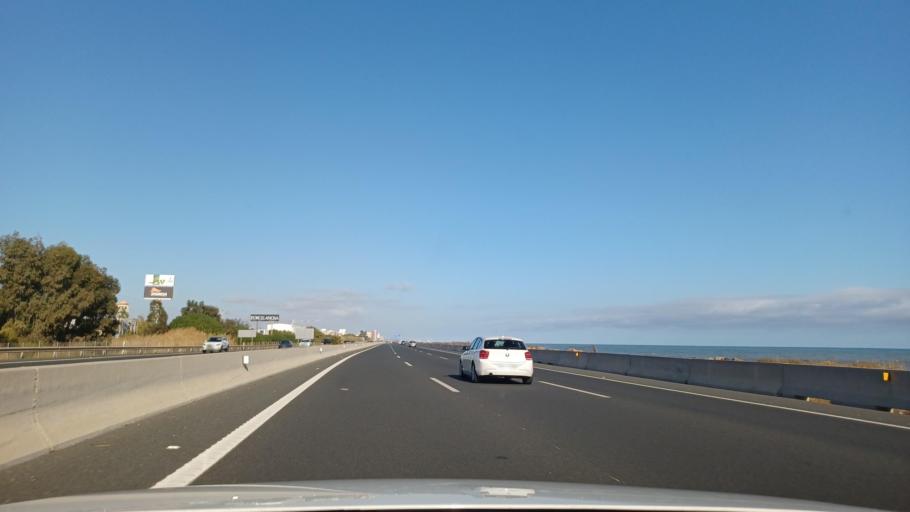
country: ES
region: Valencia
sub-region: Provincia de Valencia
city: Albuixech
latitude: 39.5352
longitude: -0.3086
